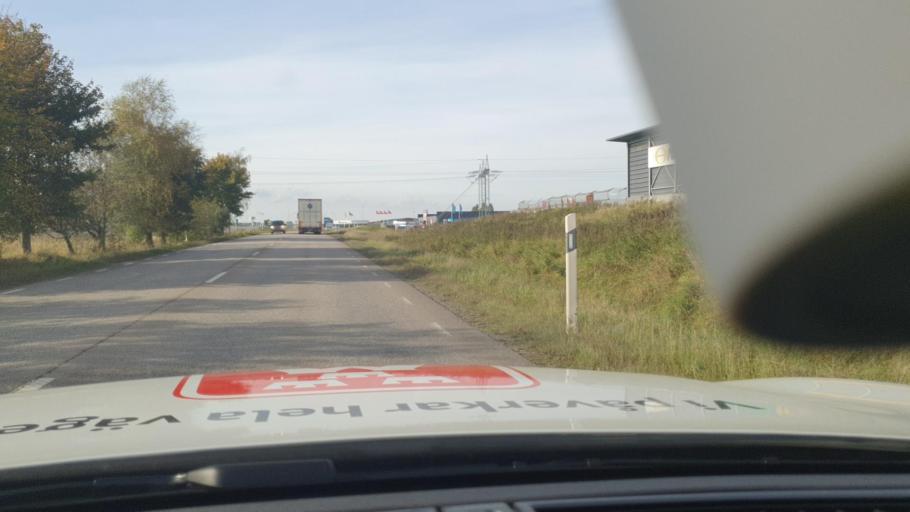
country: SE
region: Skane
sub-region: Angelholms Kommun
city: AEngelholm
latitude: 56.2525
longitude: 12.9129
